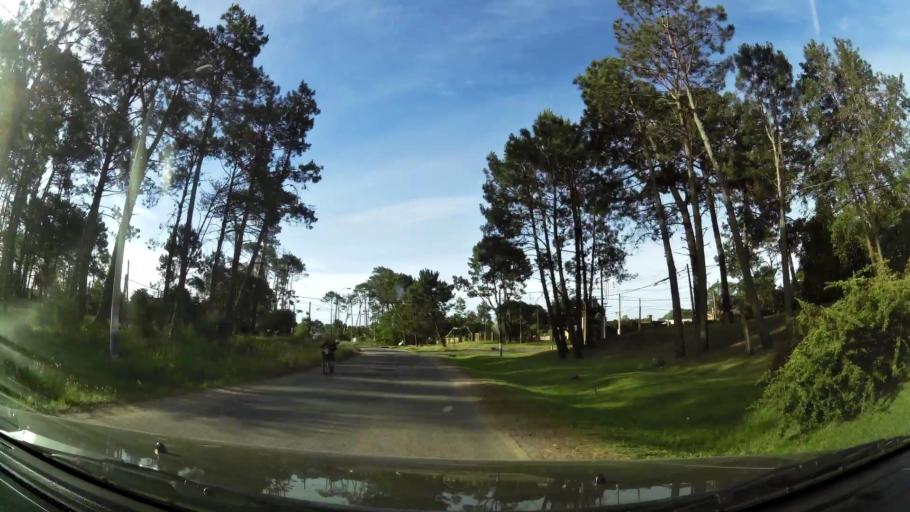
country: UY
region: Canelones
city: Empalme Olmos
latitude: -34.7807
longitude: -55.8527
